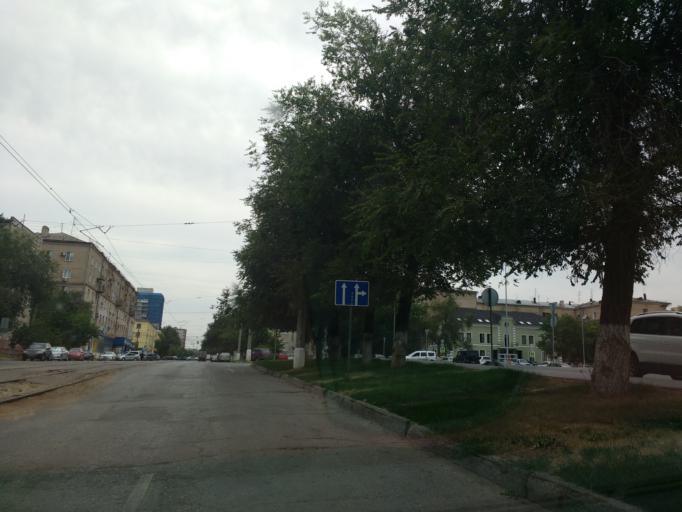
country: RU
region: Volgograd
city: Volgograd
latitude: 48.6915
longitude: 44.4947
